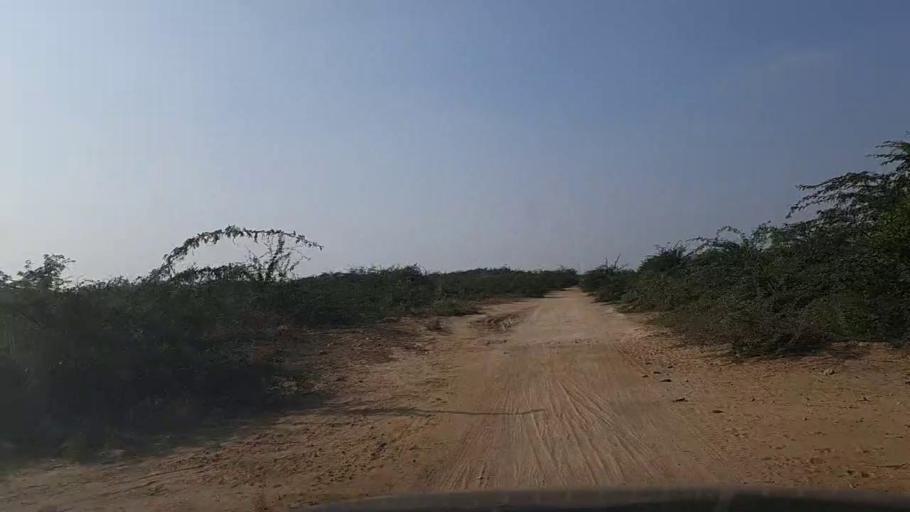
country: PK
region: Sindh
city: Gharo
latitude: 24.7492
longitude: 67.5580
